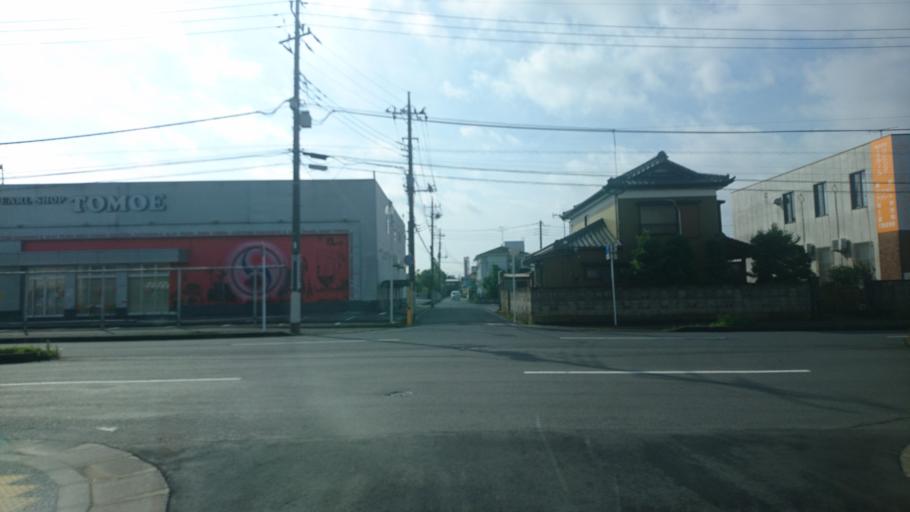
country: JP
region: Chiba
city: Katori-shi
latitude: 35.8980
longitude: 140.4953
